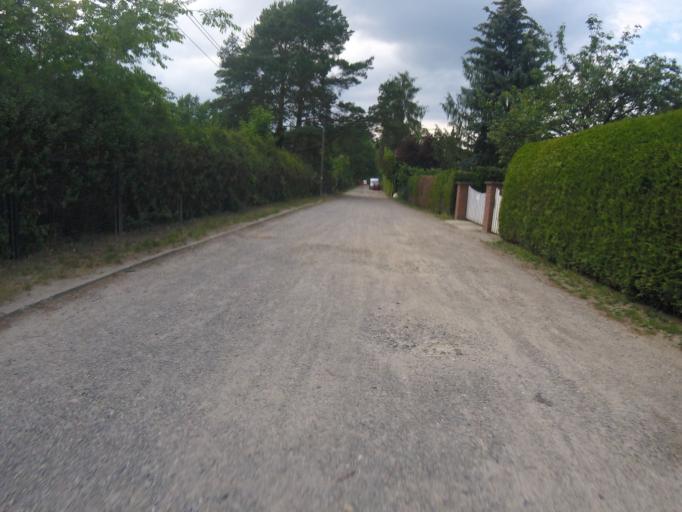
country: DE
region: Brandenburg
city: Bestensee
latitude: 52.2617
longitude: 13.6148
